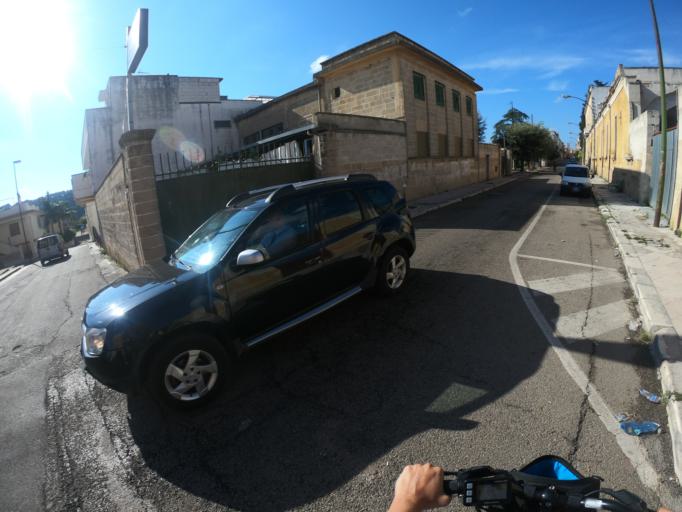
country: IT
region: Apulia
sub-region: Provincia di Lecce
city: Supersano
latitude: 40.0159
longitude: 18.2410
